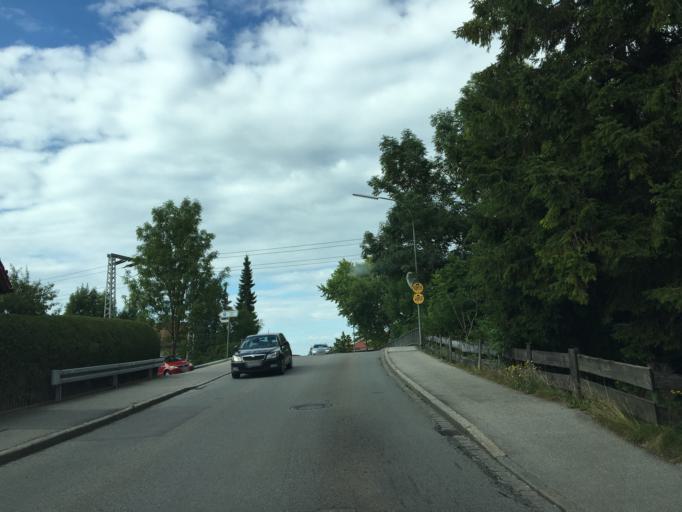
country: DE
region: Bavaria
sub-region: Upper Bavaria
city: Holzkirchen
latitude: 47.8796
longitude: 11.7020
